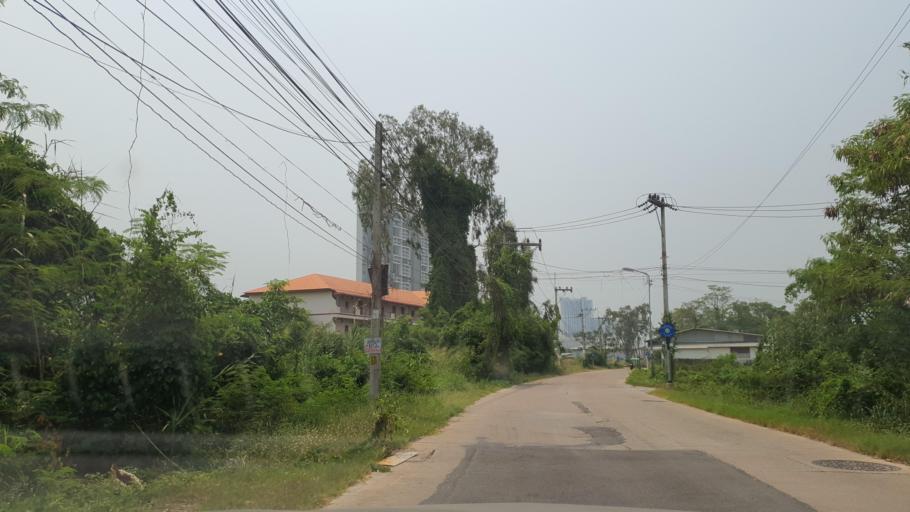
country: TH
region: Chon Buri
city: Phatthaya
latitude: 12.8807
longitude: 100.8908
